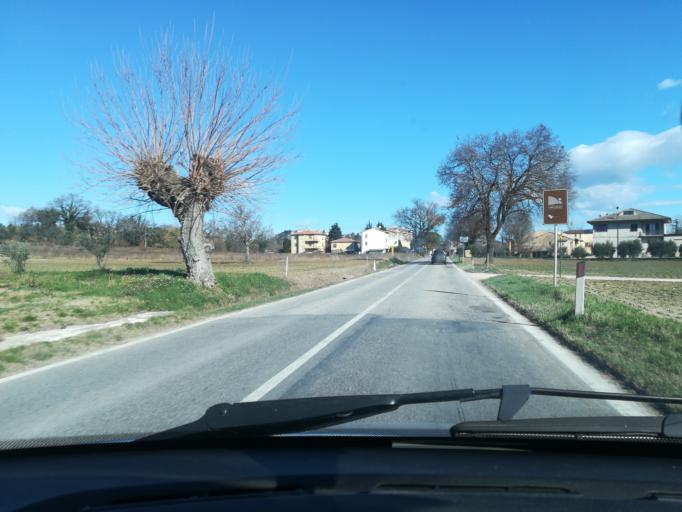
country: IT
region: The Marches
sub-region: Provincia di Macerata
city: Villa Potenza
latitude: 43.3428
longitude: 13.4318
